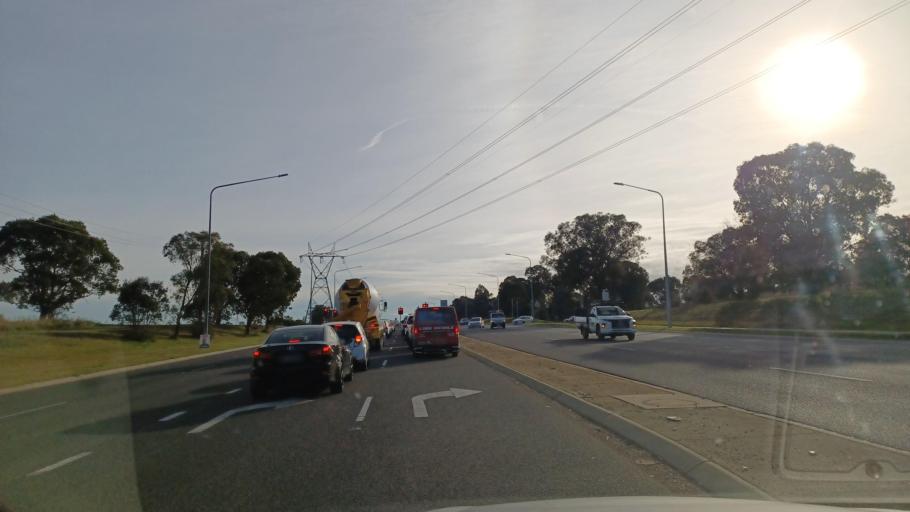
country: AU
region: Australian Capital Territory
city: Kaleen
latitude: -35.2193
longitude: 149.1306
